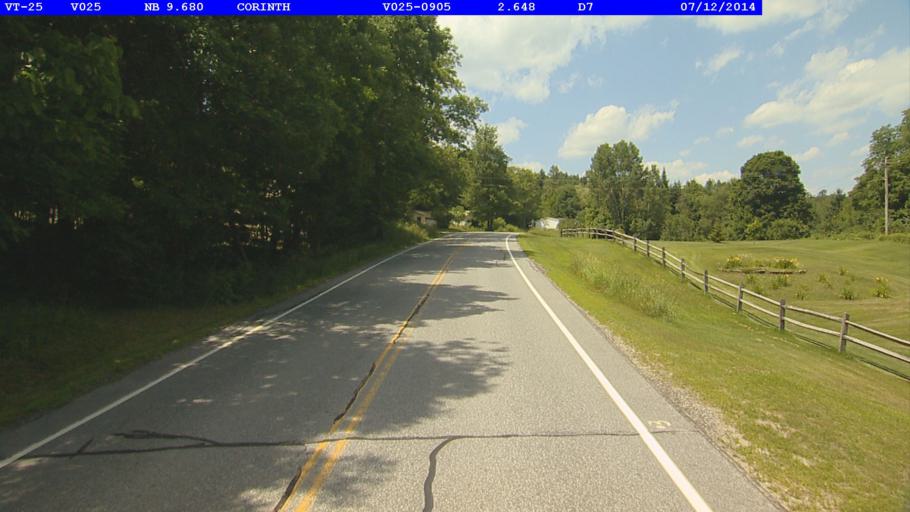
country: US
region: New Hampshire
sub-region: Grafton County
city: Haverhill
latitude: 44.0652
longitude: -72.2423
